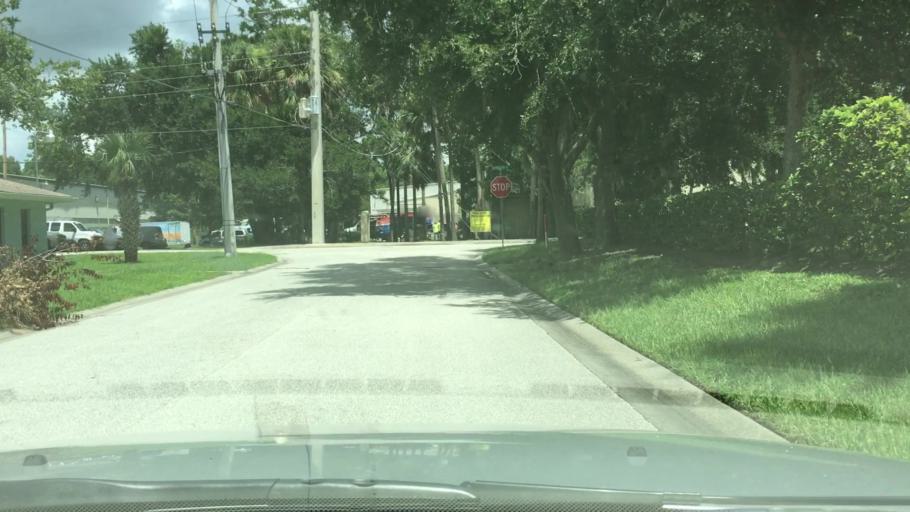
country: US
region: Florida
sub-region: Volusia County
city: Ormond Beach
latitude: 29.2736
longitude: -81.0606
